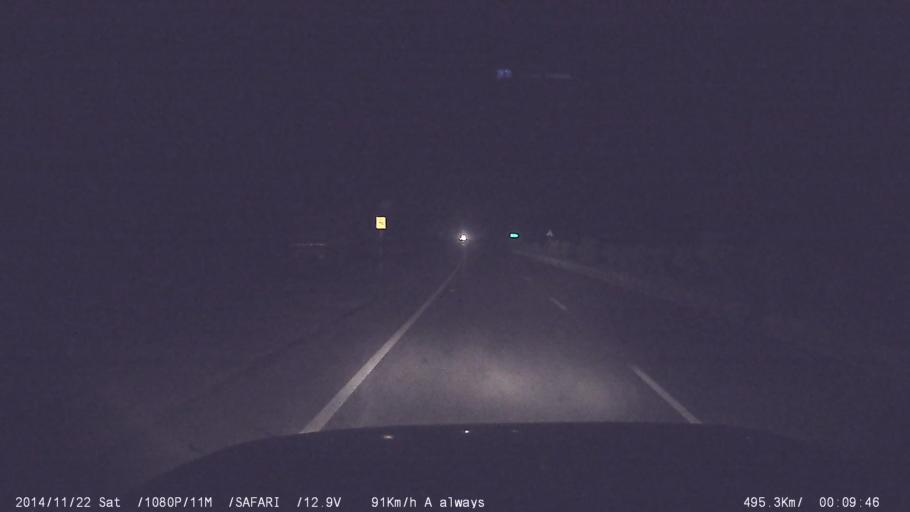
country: IN
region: Tamil Nadu
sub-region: Villupuram
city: Kallakkurichchi
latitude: 11.7385
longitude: 79.0510
